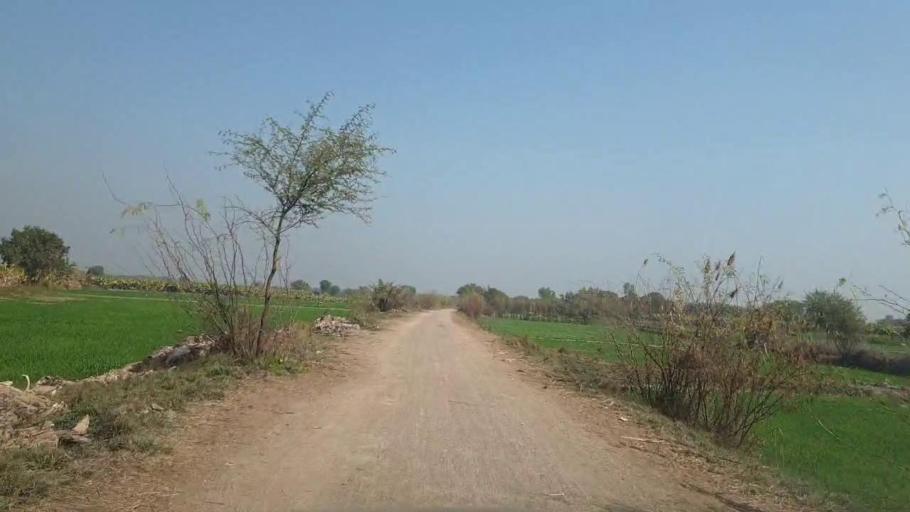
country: PK
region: Sindh
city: Matiari
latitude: 25.5470
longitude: 68.4891
